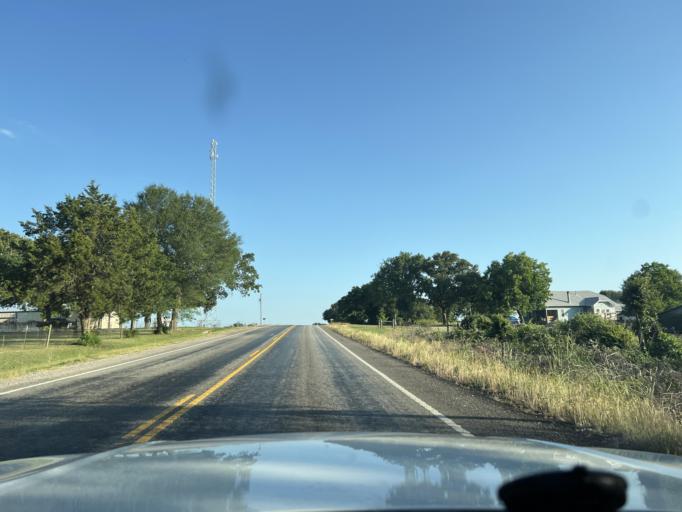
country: US
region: Texas
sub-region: Washington County
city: Brenham
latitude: 30.2104
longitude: -96.3637
